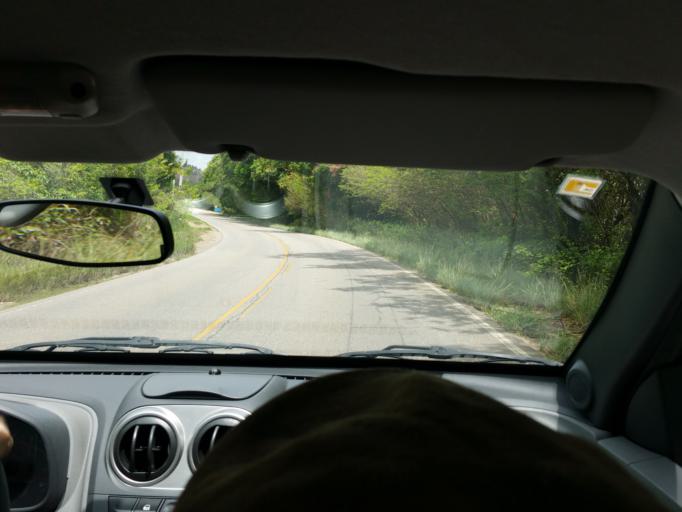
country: BR
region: Pernambuco
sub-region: Sirinhaem
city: Sirinhaem
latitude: -8.6412
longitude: -35.1182
